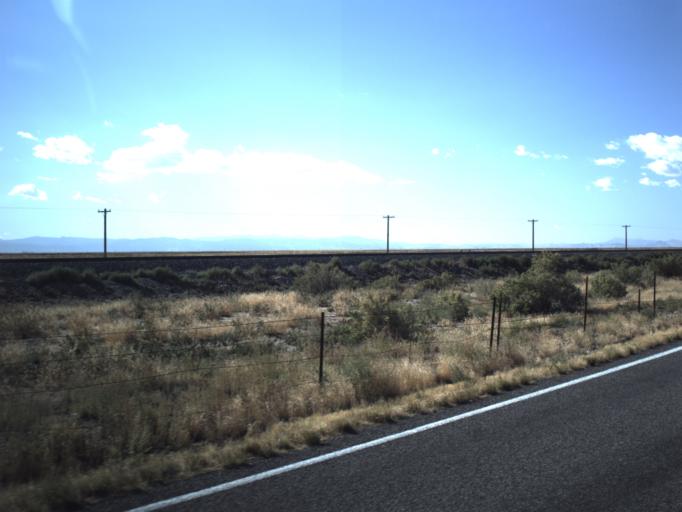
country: US
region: Utah
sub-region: Millard County
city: Delta
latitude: 39.2051
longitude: -112.6849
